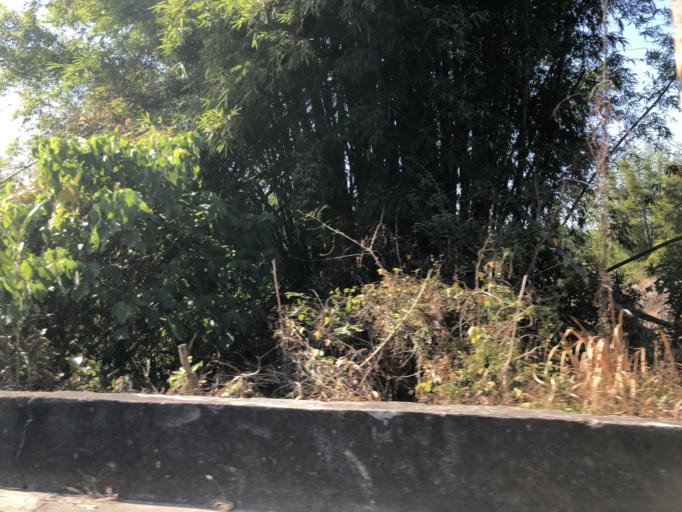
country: TW
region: Taiwan
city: Yujing
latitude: 23.0549
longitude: 120.4000
